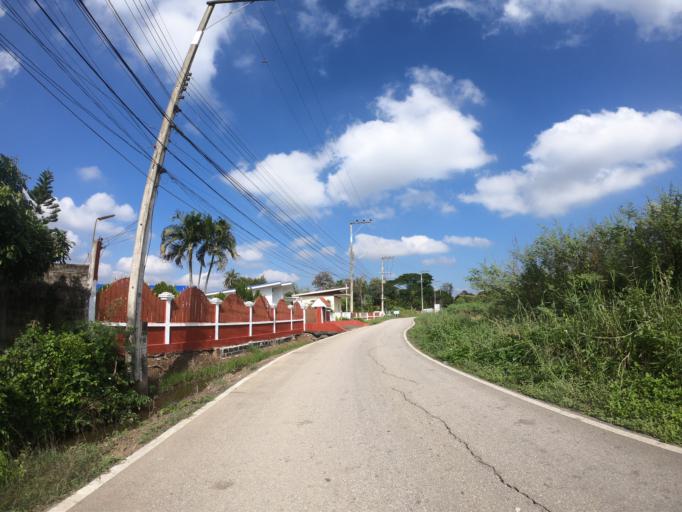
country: TH
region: Chiang Mai
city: Saraphi
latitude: 18.7203
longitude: 99.0191
